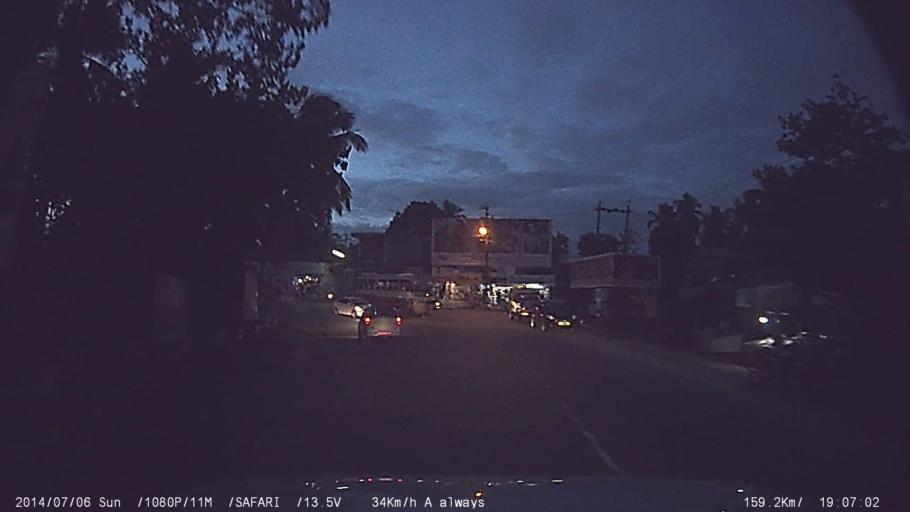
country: IN
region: Kerala
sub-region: Palakkad district
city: Palakkad
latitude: 10.7484
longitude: 76.6530
